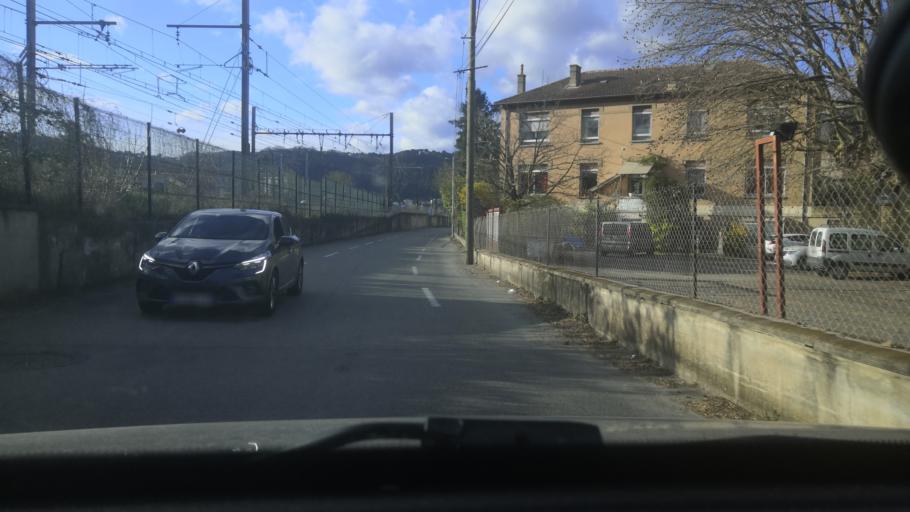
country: FR
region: Rhone-Alpes
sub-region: Departement de l'Ardeche
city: Le Teil
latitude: 44.5407
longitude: 4.6898
